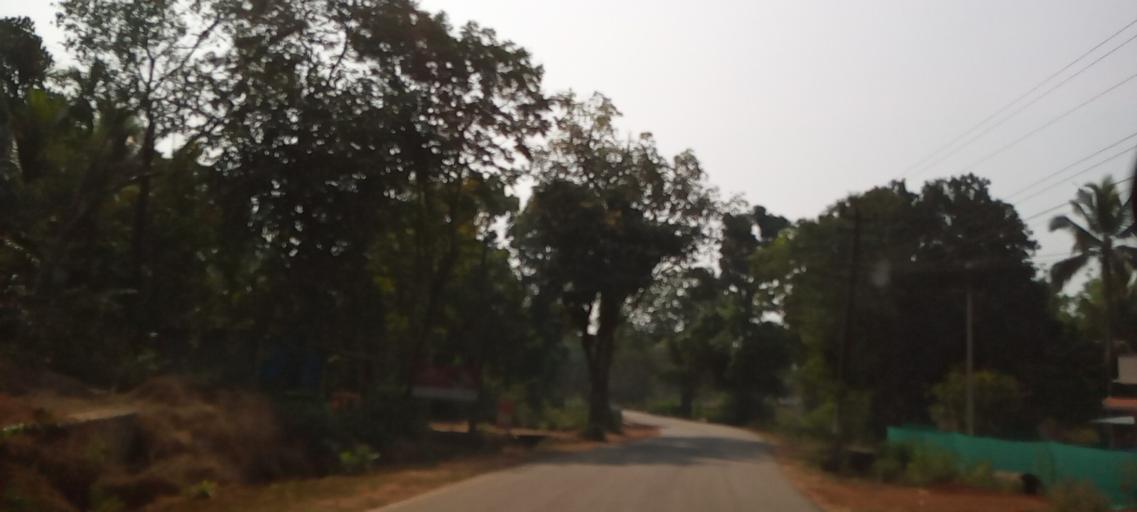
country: IN
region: Karnataka
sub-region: Udupi
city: Someshwar
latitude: 13.5221
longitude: 74.9289
